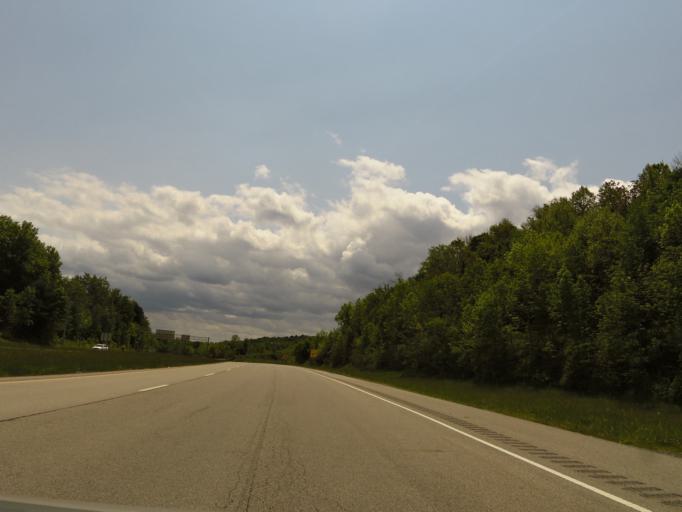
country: US
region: Ohio
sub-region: Meigs County
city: Pomeroy
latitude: 39.0563
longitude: -82.0171
